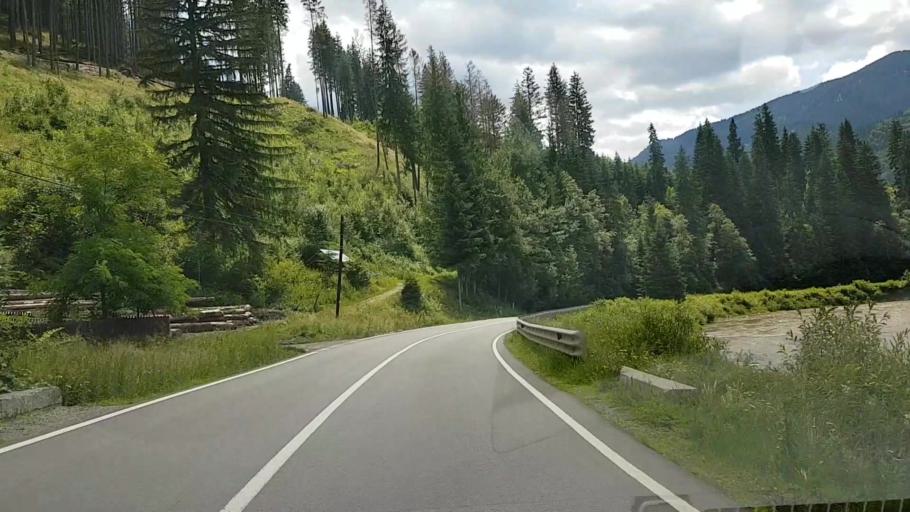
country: RO
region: Suceava
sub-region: Comuna Crucea
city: Crucea
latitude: 47.3541
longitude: 25.6156
